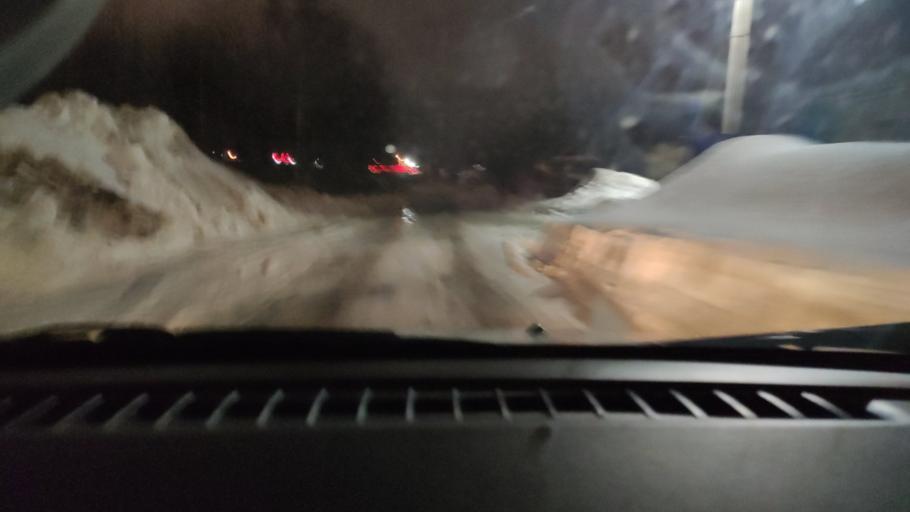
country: RU
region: Perm
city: Froly
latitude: 57.9397
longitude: 56.2635
